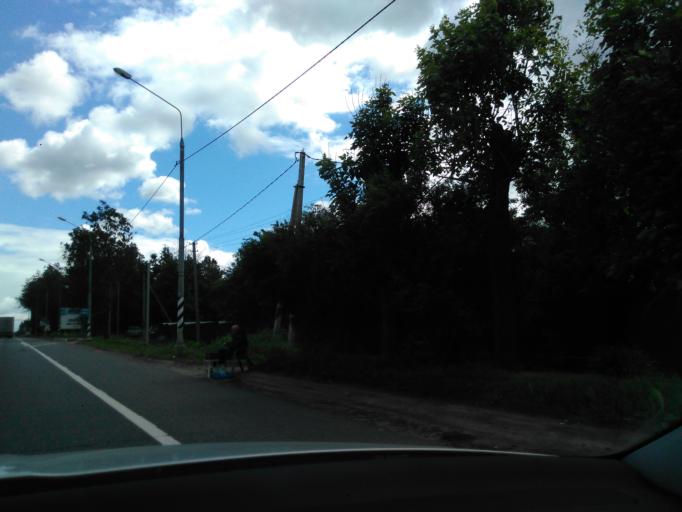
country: RU
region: Moskovskaya
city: Klin
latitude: 56.2812
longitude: 36.8261
